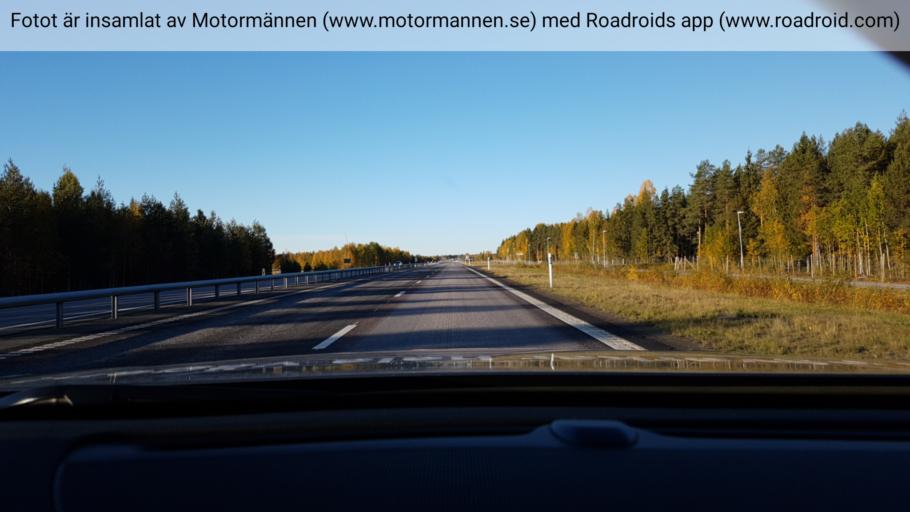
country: SE
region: Norrbotten
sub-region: Lulea Kommun
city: Sodra Sunderbyn
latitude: 65.5426
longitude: 21.8274
